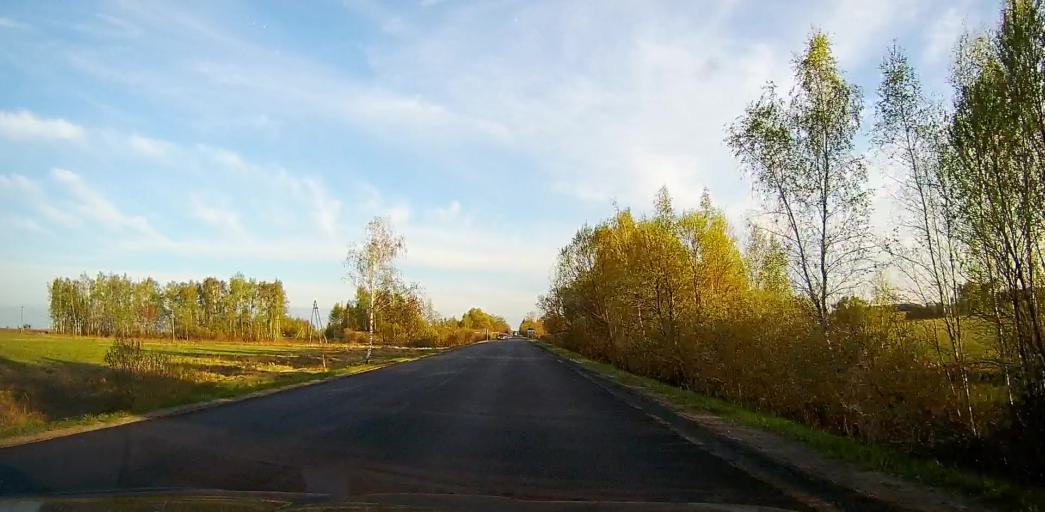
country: RU
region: Moskovskaya
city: Bronnitsy
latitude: 55.2801
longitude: 38.2182
